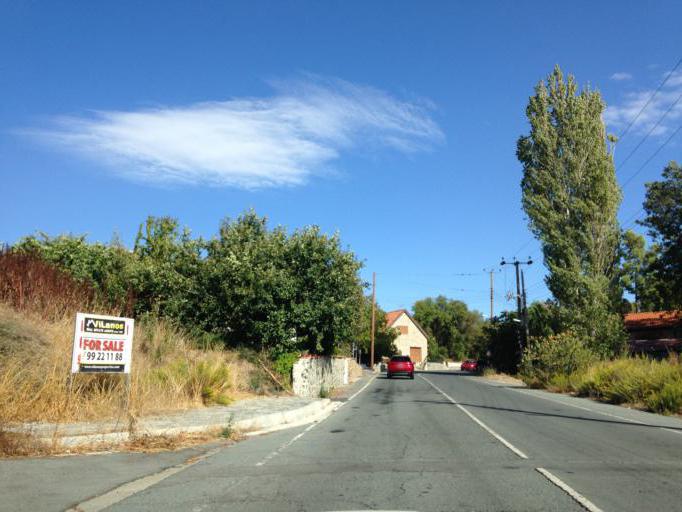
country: CY
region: Limassol
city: Pelendri
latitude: 34.8819
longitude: 32.8559
